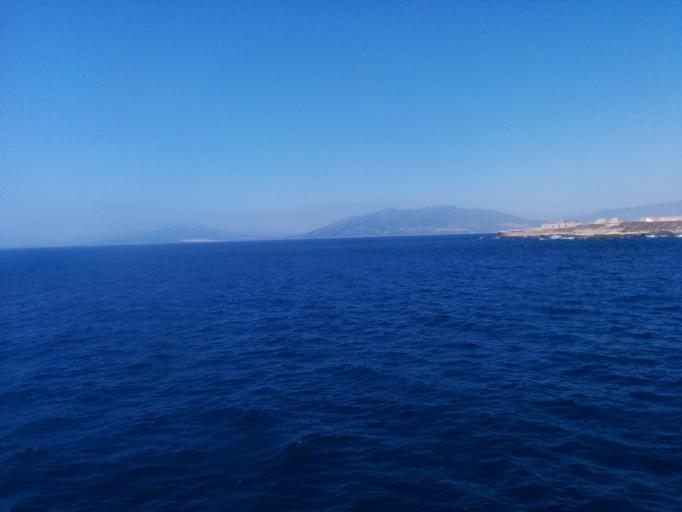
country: ES
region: Andalusia
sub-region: Provincia de Cadiz
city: Tarifa
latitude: 35.9960
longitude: -5.6103
